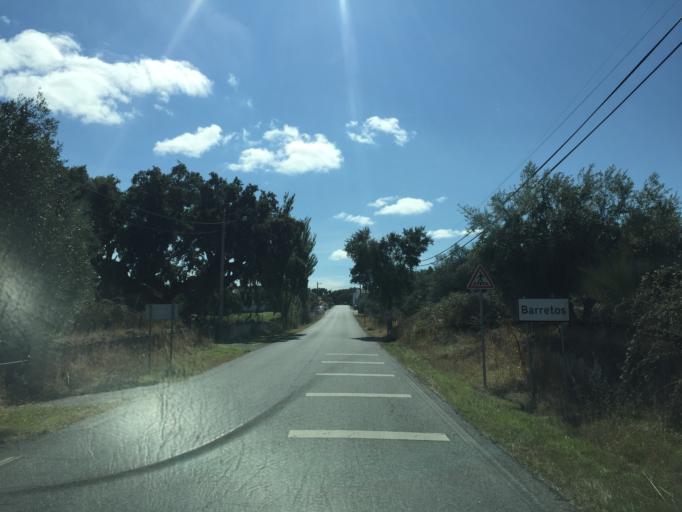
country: PT
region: Portalegre
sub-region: Marvao
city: Marvao
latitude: 39.4362
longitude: -7.3645
